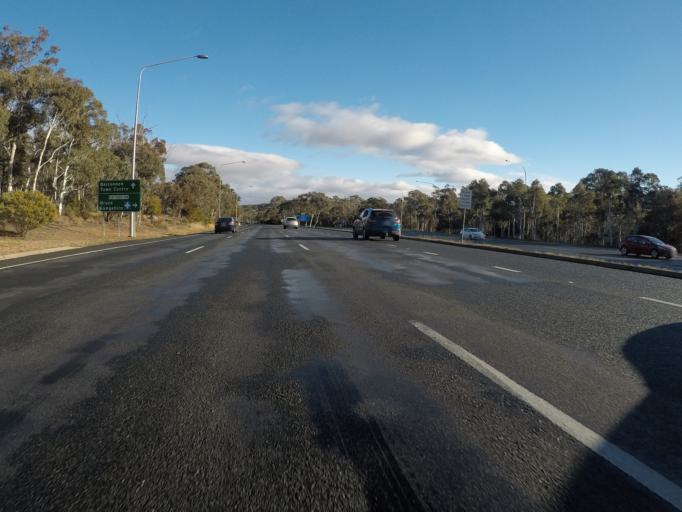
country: AU
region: Australian Capital Territory
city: Macquarie
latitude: -35.2565
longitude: 149.0888
